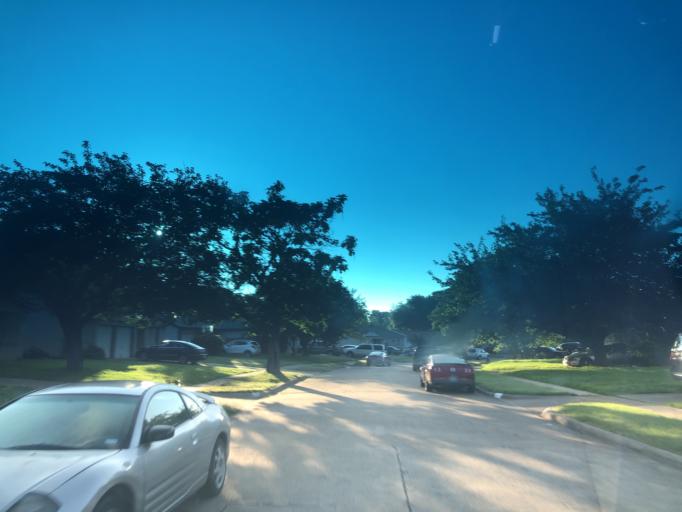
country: US
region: Texas
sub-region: Dallas County
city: Grand Prairie
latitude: 32.7058
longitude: -97.0145
